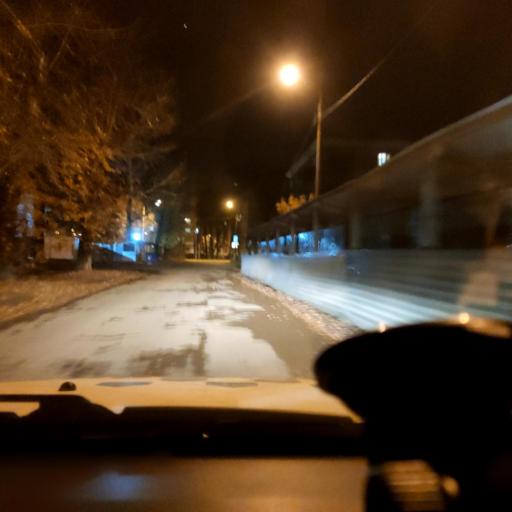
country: RU
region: Perm
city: Perm
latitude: 58.0269
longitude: 56.2897
